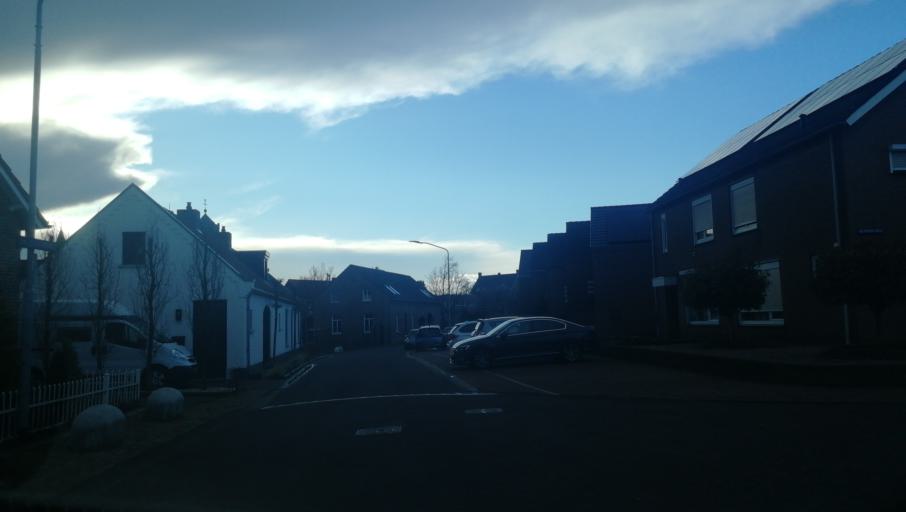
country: NL
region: Limburg
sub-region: Gemeente Venlo
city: Tegelen
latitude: 51.3579
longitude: 6.1309
